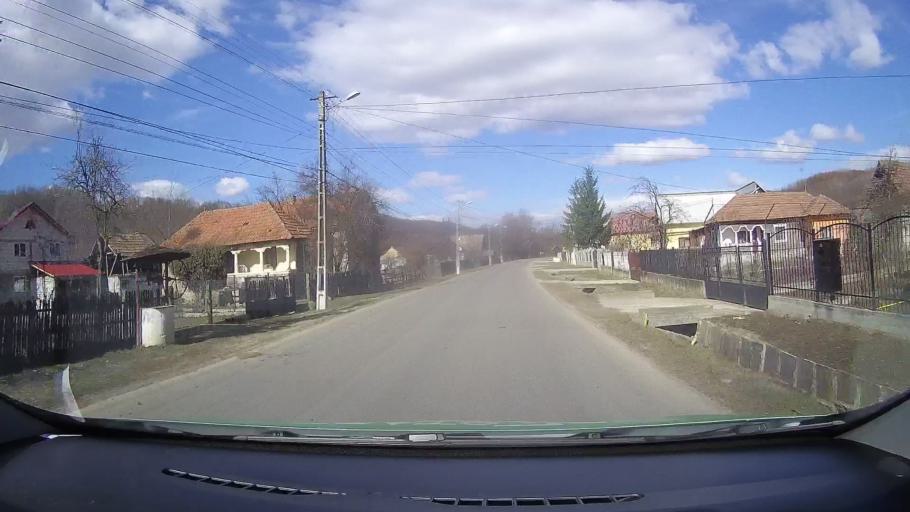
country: RO
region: Dambovita
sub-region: Comuna Vulcana-Pandele
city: Gura Vulcanei
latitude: 45.0359
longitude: 25.3918
